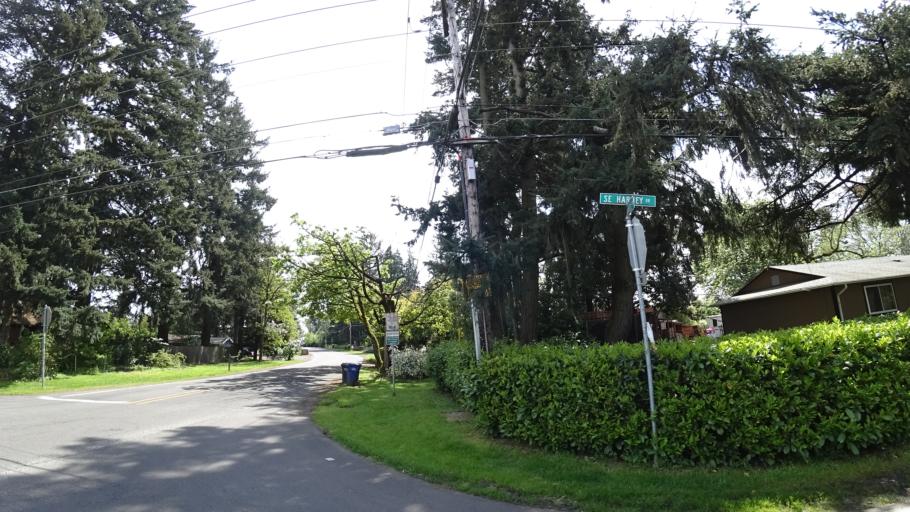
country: US
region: Oregon
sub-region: Multnomah County
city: Lents
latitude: 45.4614
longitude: -122.6017
